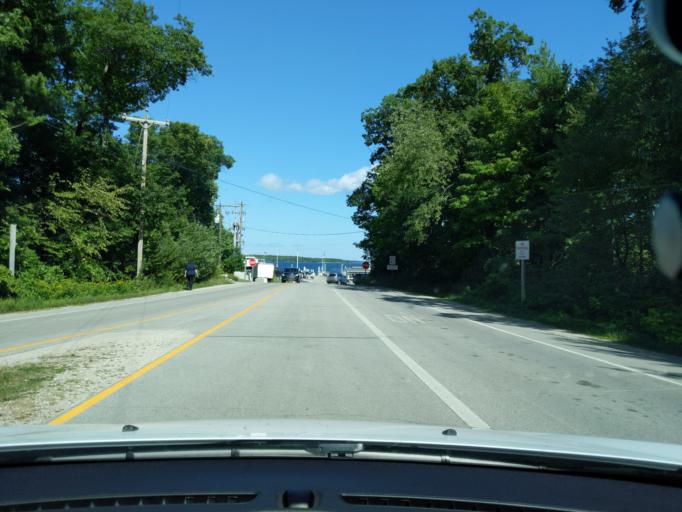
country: US
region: Michigan
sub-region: Delta County
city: Escanaba
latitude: 45.2901
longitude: -86.9788
